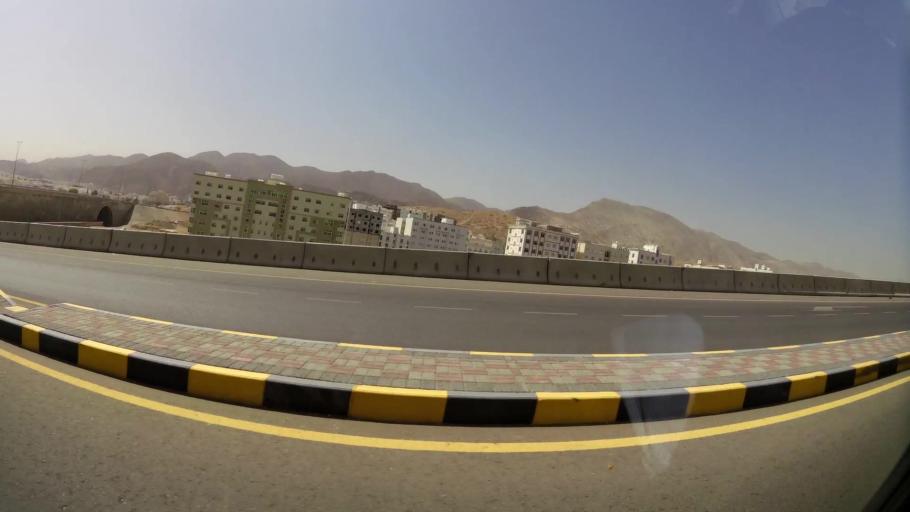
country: OM
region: Muhafazat Masqat
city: Bawshar
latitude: 23.5782
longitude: 58.4169
